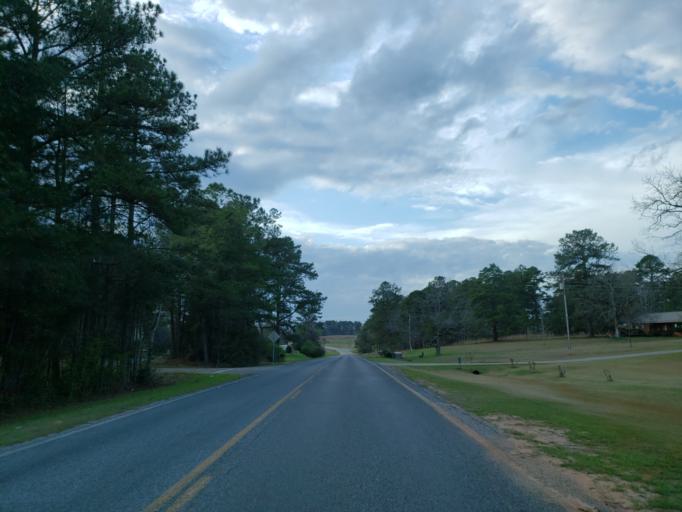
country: US
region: Mississippi
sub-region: Clarke County
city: Stonewall
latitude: 32.2083
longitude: -88.6929
